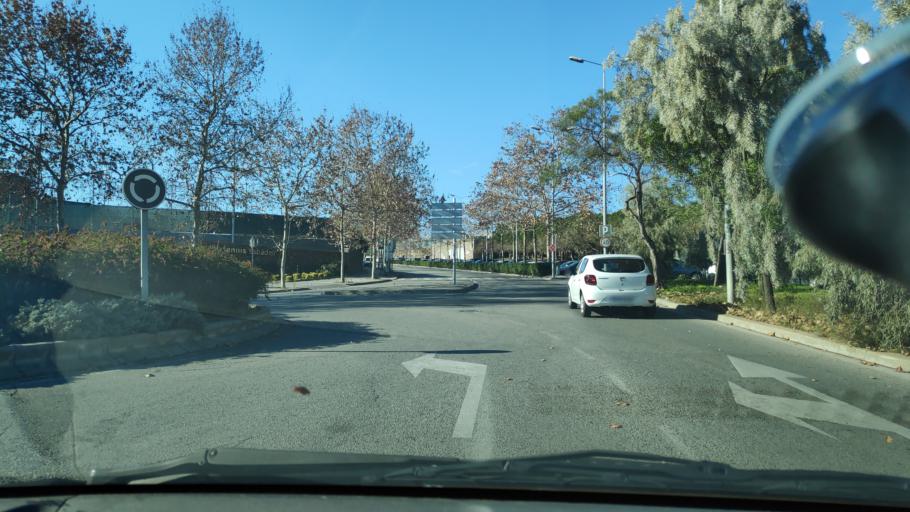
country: ES
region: Catalonia
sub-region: Provincia de Barcelona
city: Sabadell
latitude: 41.5507
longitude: 2.0953
